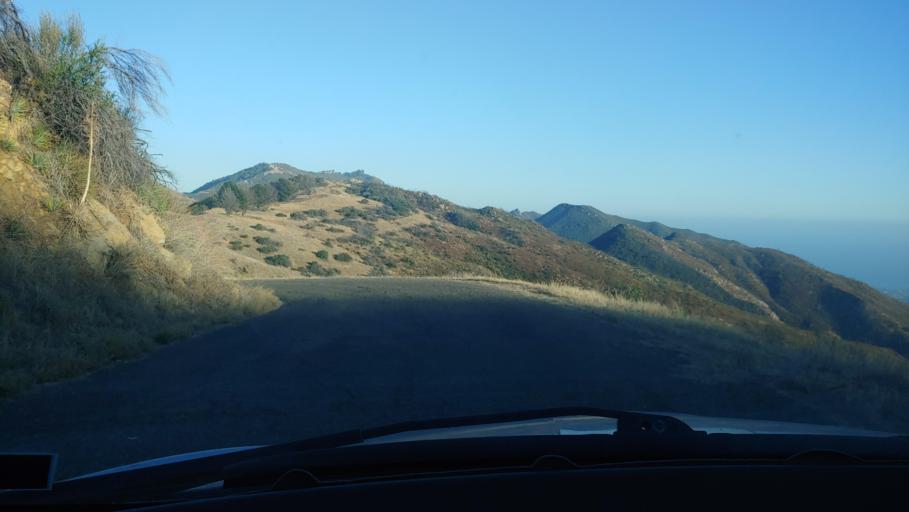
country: US
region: California
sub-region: Santa Barbara County
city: Mission Canyon
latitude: 34.5070
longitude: -119.7649
